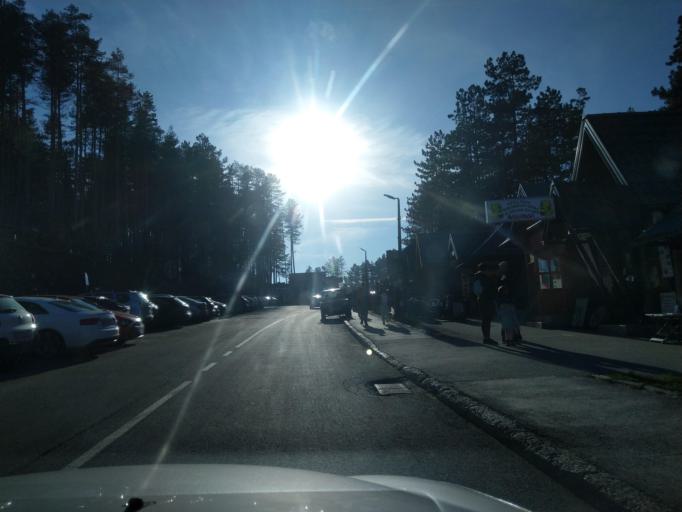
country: RS
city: Zlatibor
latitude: 43.7240
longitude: 19.6970
